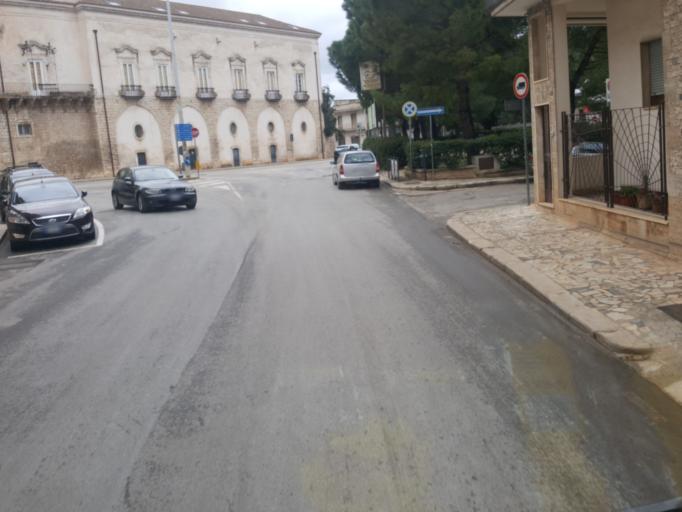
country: IT
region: Apulia
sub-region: Provincia di Bari
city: Turi
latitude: 40.9168
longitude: 17.0234
